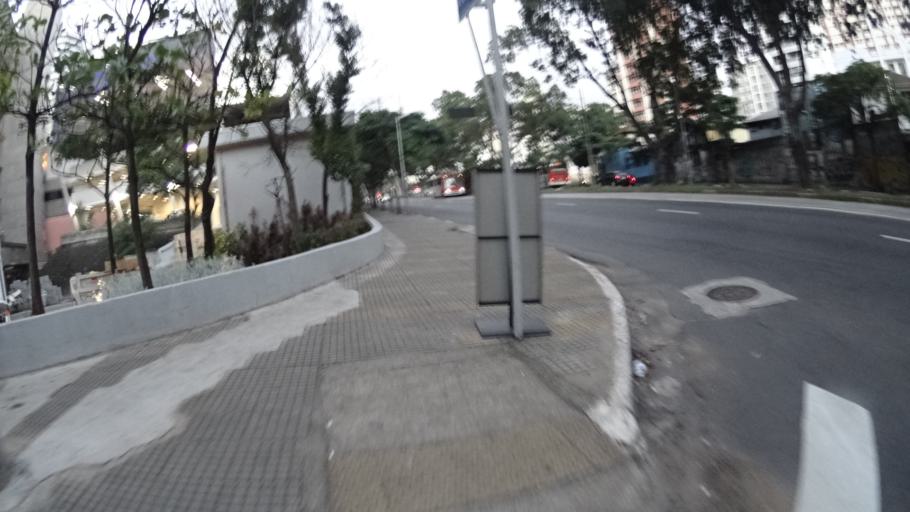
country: BR
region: Sao Paulo
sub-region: Sao Paulo
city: Sao Paulo
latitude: -23.5586
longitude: -46.6687
